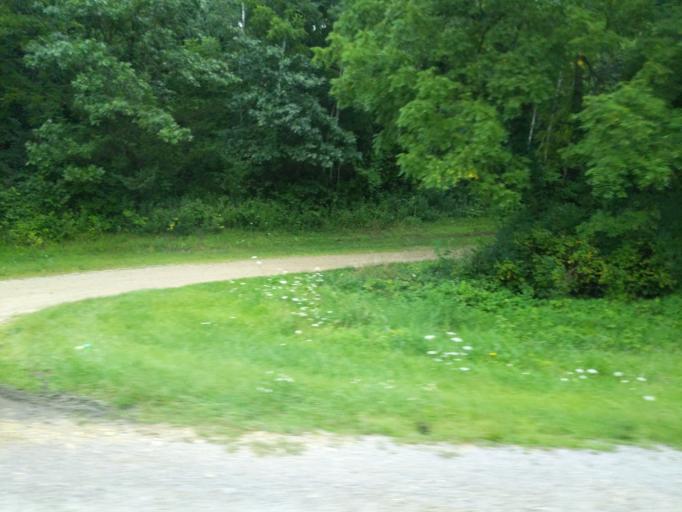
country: US
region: Wisconsin
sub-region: Sauk County
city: Sauk City
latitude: 43.2402
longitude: -89.7276
